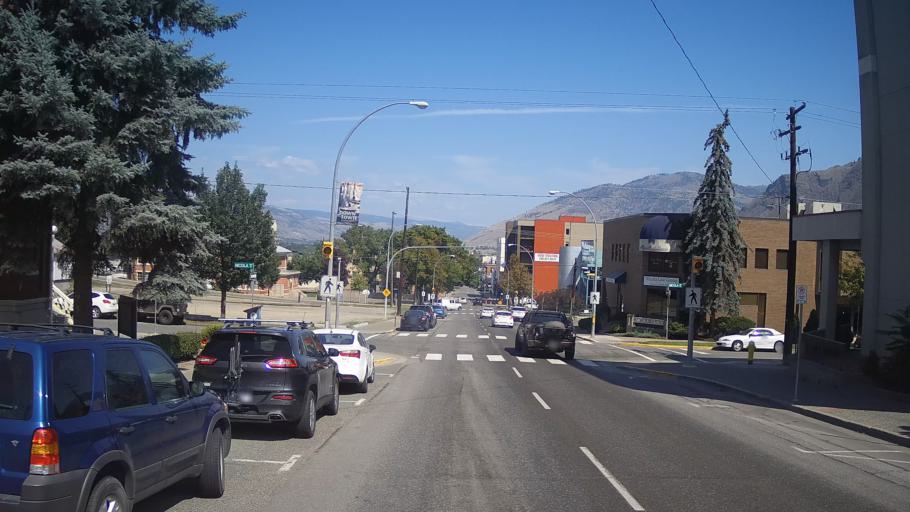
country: CA
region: British Columbia
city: Kamloops
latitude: 50.6720
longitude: -120.3345
